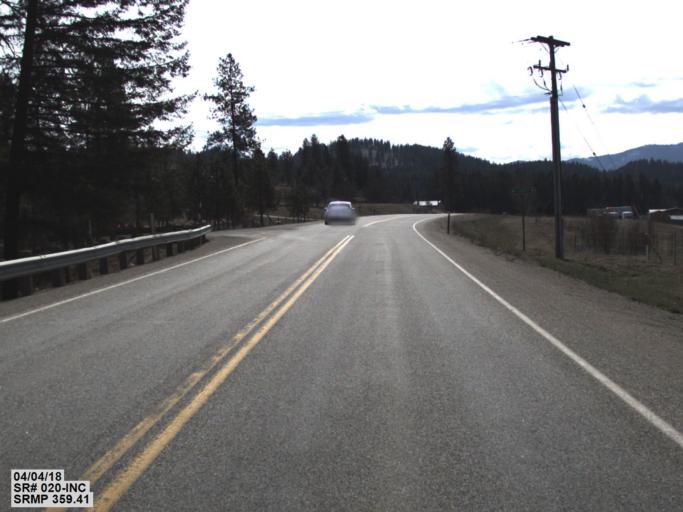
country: US
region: Washington
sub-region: Stevens County
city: Colville
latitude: 48.5236
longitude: -117.8156
